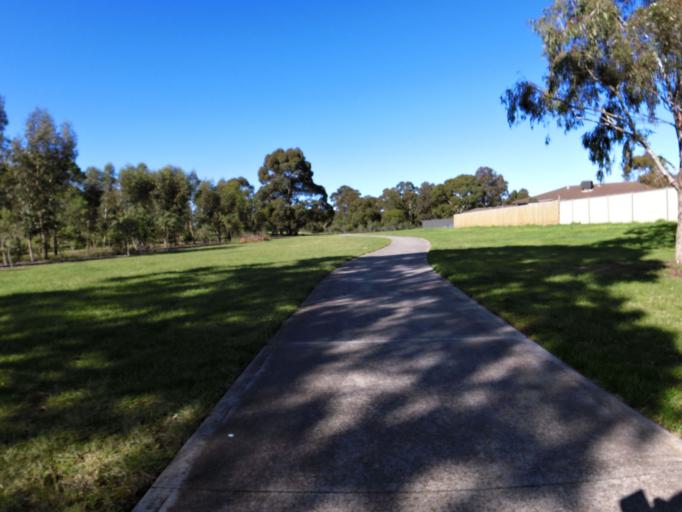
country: AU
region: Victoria
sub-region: Wyndham
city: Tarneit
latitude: -37.8799
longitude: 144.6770
